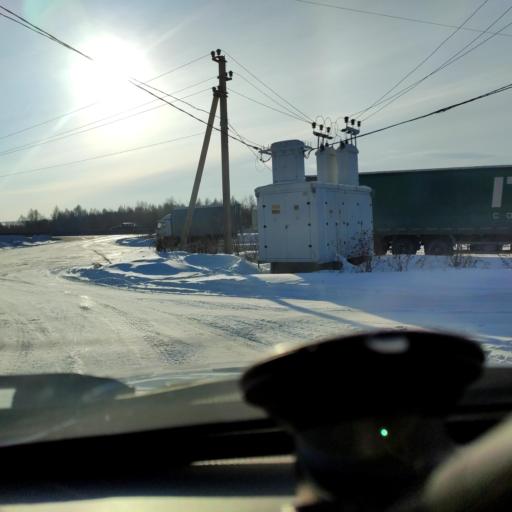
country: RU
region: Perm
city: Froly
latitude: 57.9347
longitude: 56.2096
